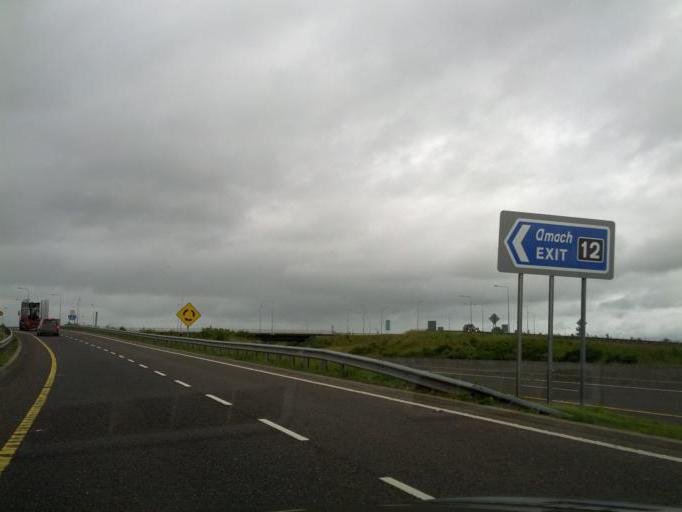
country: IE
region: Munster
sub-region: An Clar
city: Ennis
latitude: 52.8253
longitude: -8.9385
